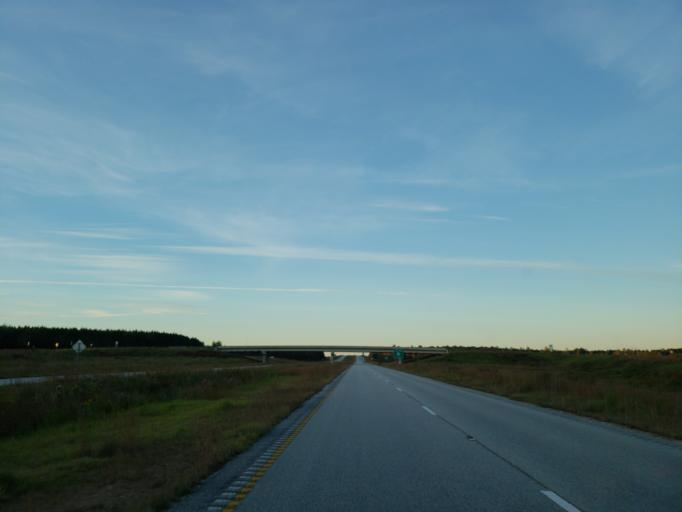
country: US
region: Mississippi
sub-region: Wayne County
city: Belmont
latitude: 31.4339
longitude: -88.4656
